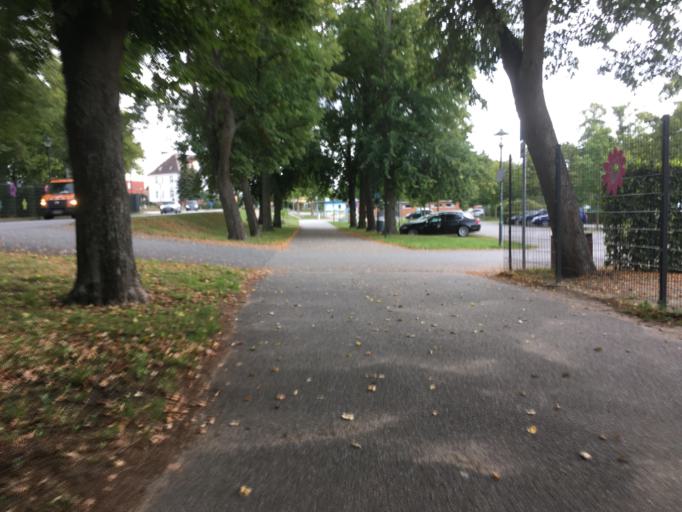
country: DE
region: Brandenburg
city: Prenzlau
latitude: 53.3075
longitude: 13.8598
